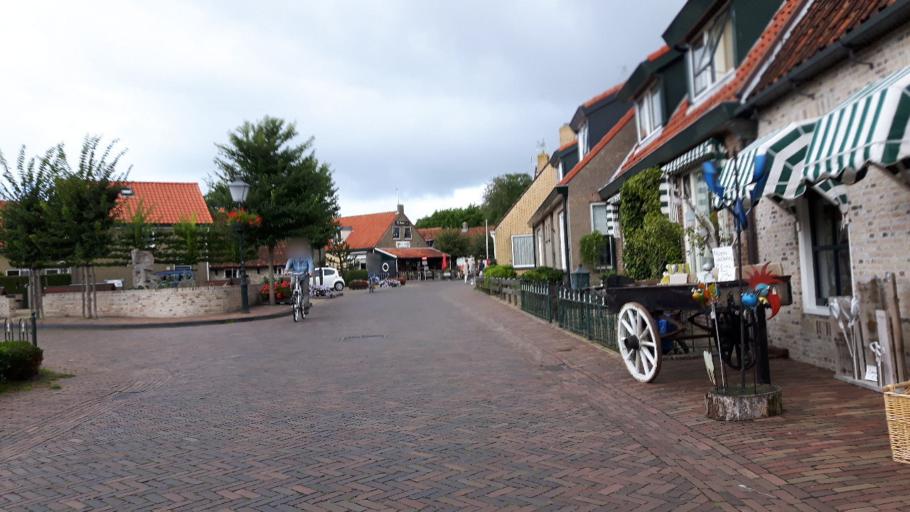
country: NL
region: Friesland
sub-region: Gemeente Ameland
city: Hollum
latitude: 53.4403
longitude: 5.6392
